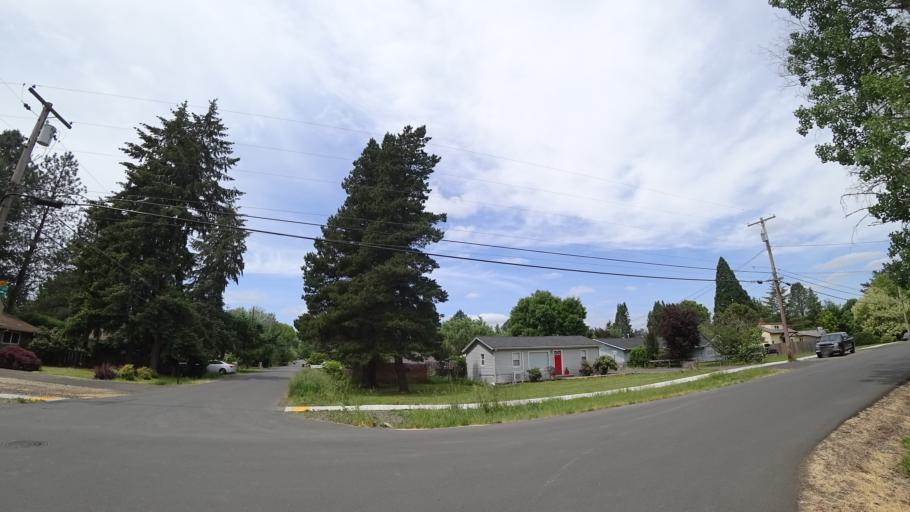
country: US
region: Oregon
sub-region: Washington County
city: Metzger
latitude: 45.4481
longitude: -122.7693
